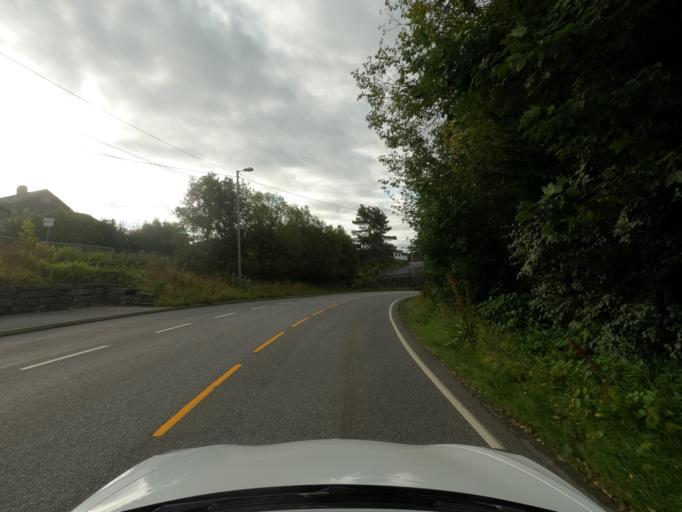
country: NO
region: Hordaland
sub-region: Bergen
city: Sandsli
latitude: 60.3134
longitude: 5.2895
